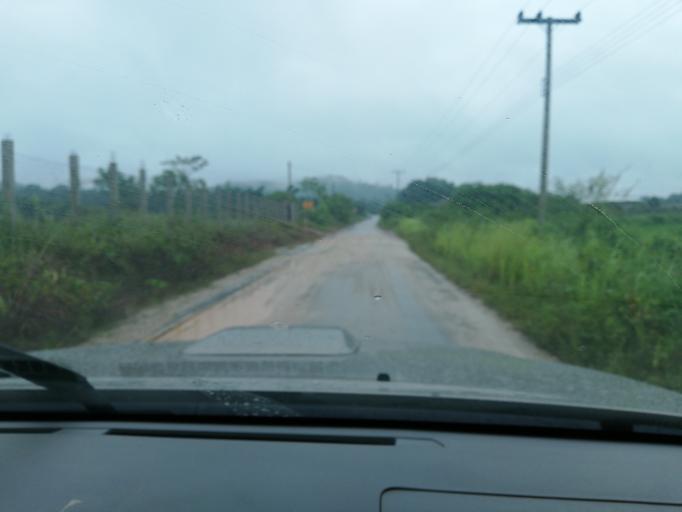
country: LA
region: Loungnamtha
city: Louang Namtha
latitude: 20.9796
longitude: 101.3860
